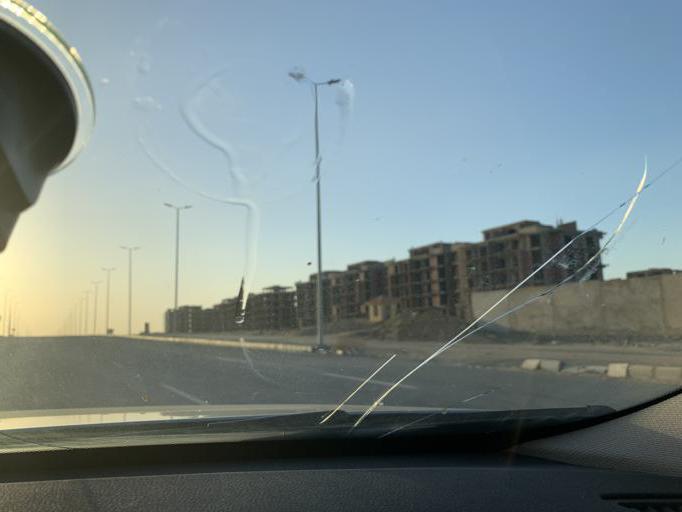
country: EG
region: Muhafazat al Qalyubiyah
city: Al Khankah
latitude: 30.0228
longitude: 31.5919
